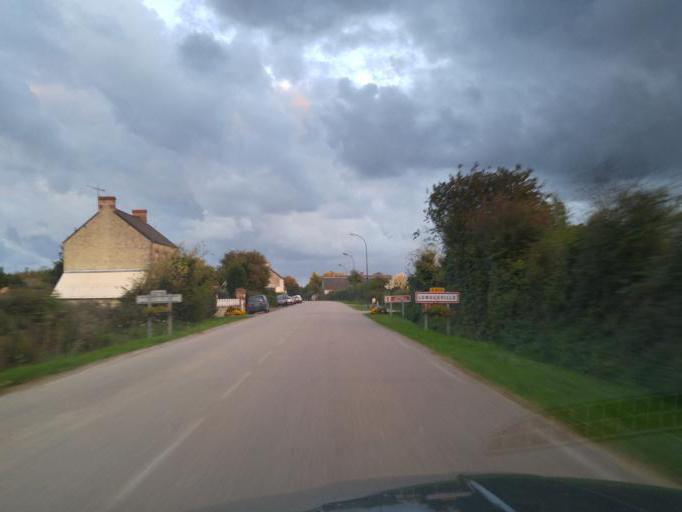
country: FR
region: Lower Normandy
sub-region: Departement du Calvados
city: Grandcamp-Maisy
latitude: 49.3410
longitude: -0.9721
